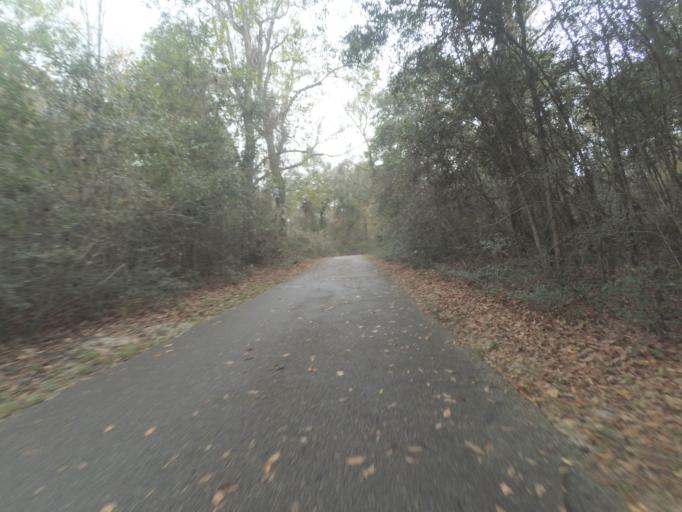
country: US
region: Florida
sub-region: Alachua County
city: Gainesville
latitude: 29.6077
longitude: -82.2735
